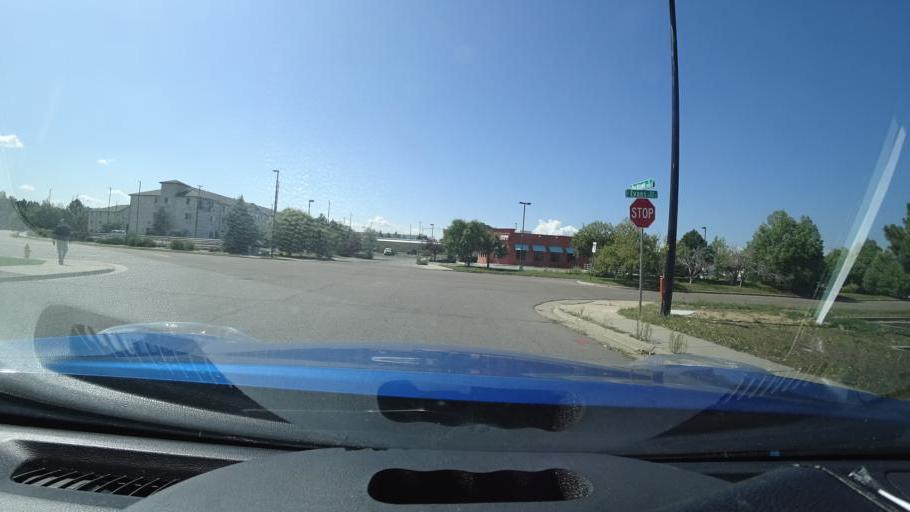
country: US
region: Colorado
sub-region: Adams County
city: Aurora
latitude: 39.6795
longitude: -104.8258
